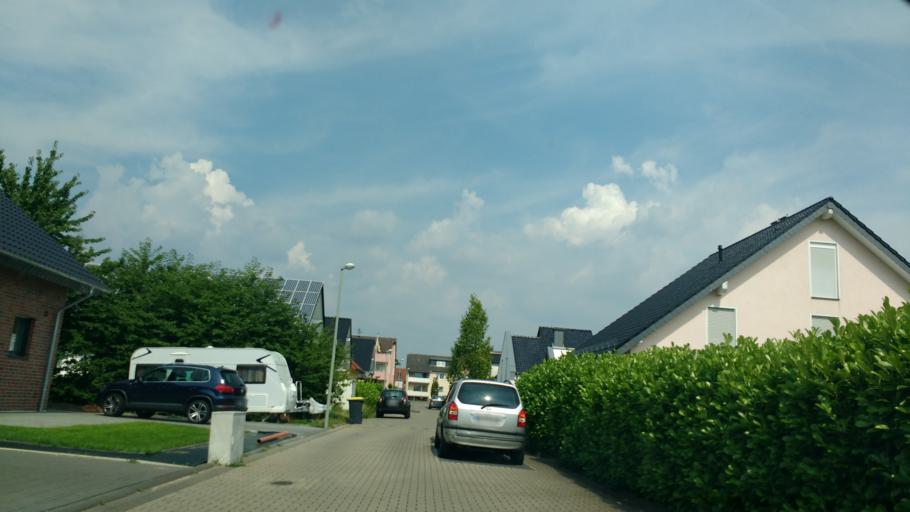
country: DE
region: North Rhine-Westphalia
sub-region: Regierungsbezirk Detmold
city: Paderborn
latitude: 51.7553
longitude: 8.7287
